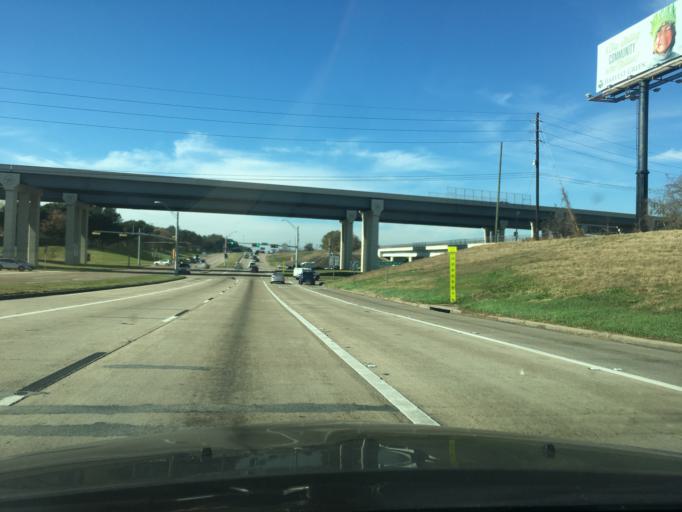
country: US
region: Texas
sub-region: Fort Bend County
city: New Territory
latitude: 29.6018
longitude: -95.6831
